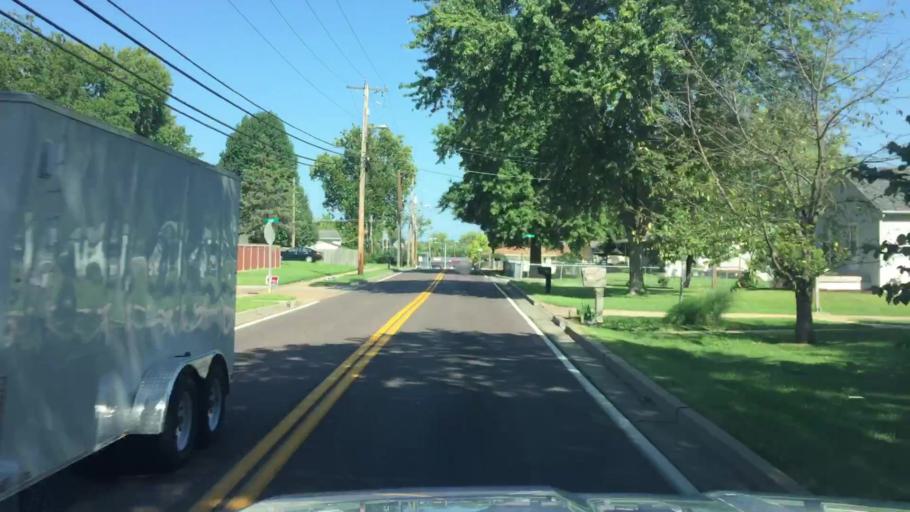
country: US
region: Missouri
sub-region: Jefferson County
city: Arnold
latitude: 38.4512
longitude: -90.3600
